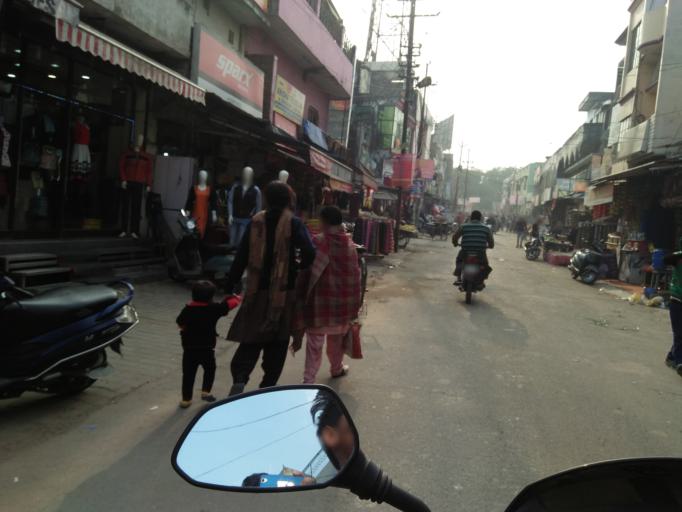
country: IN
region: Uttar Pradesh
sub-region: Moradabad
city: Moradabad
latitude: 28.8621
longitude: 78.7526
